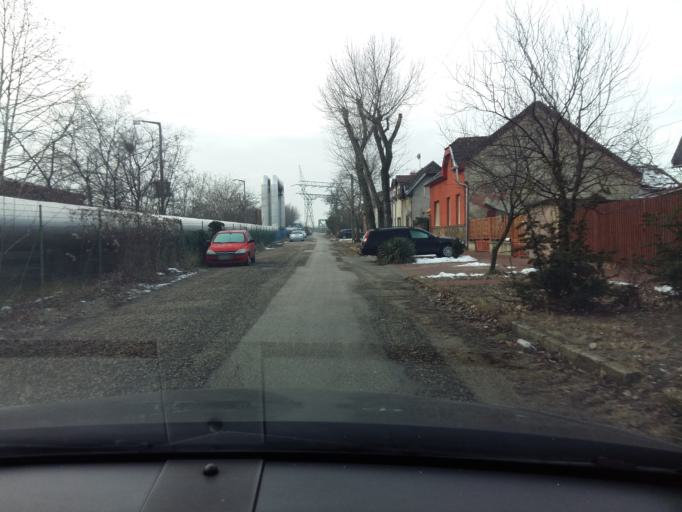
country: HU
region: Budapest
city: Budapest IV. keruelet
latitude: 47.5465
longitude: 19.1001
